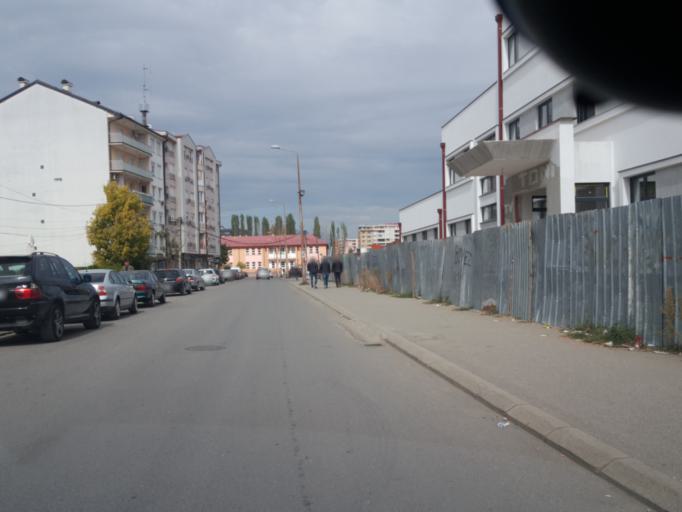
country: XK
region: Gjakova
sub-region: Komuna e Gjakoves
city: Gjakove
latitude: 42.3827
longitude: 20.4347
